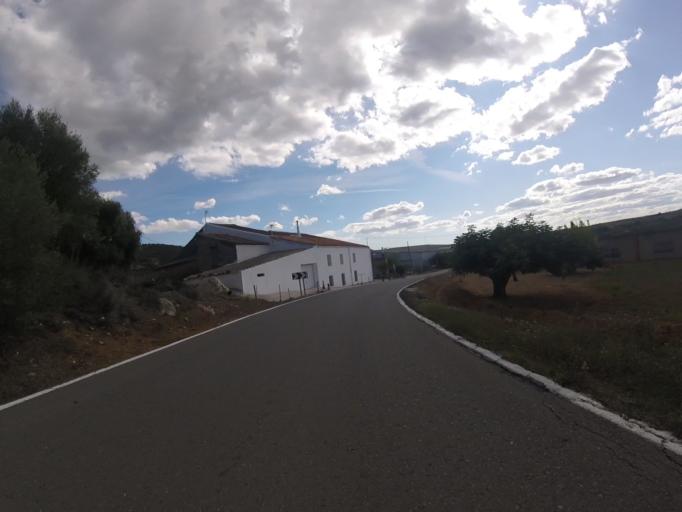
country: ES
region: Valencia
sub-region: Provincia de Castello
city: Cuevas de Vinroma
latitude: 40.3512
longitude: 0.1279
